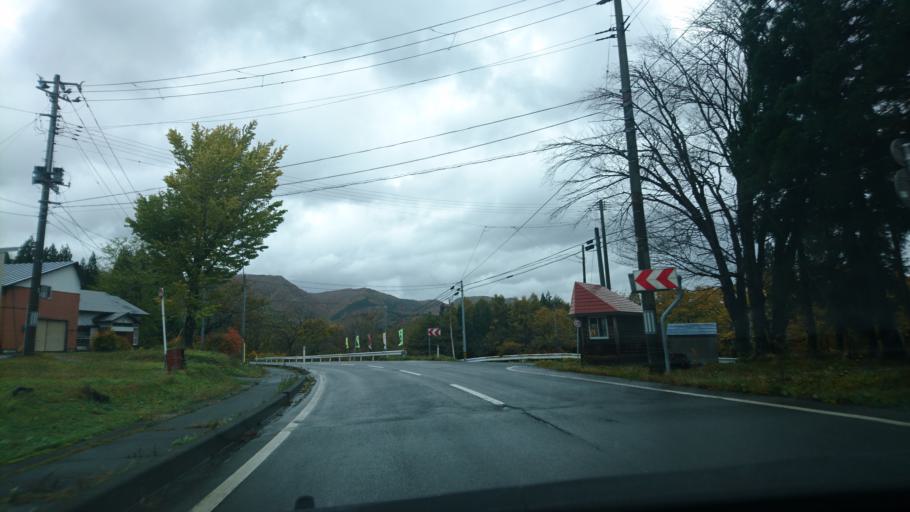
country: JP
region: Akita
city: Kakunodatemachi
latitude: 39.4696
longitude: 140.7815
